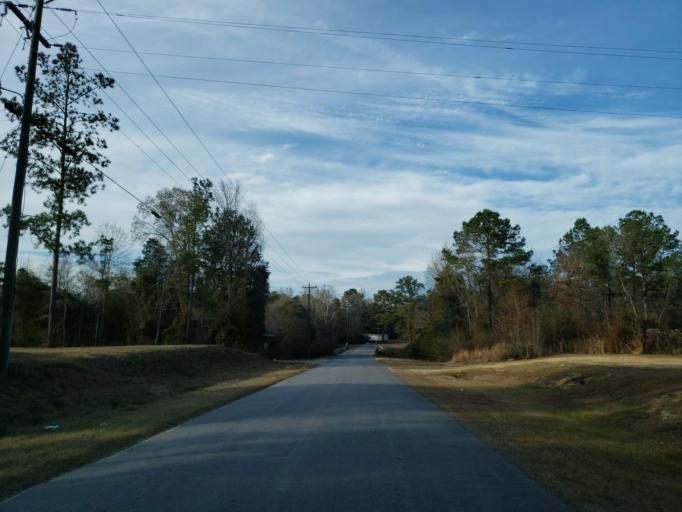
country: US
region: Mississippi
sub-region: Wayne County
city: Belmont
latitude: 31.5030
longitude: -88.5073
